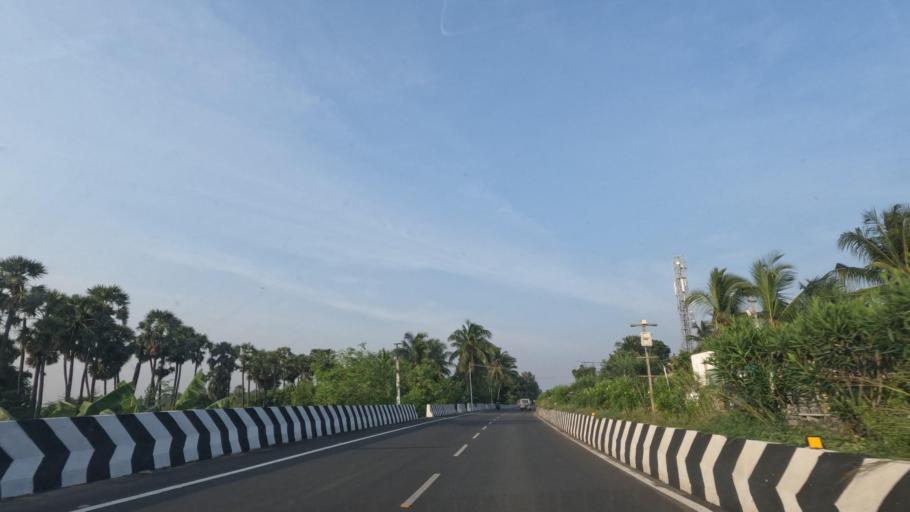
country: IN
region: Tamil Nadu
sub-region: Kancheepuram
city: Mamallapuram
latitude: 12.6512
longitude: 80.2046
